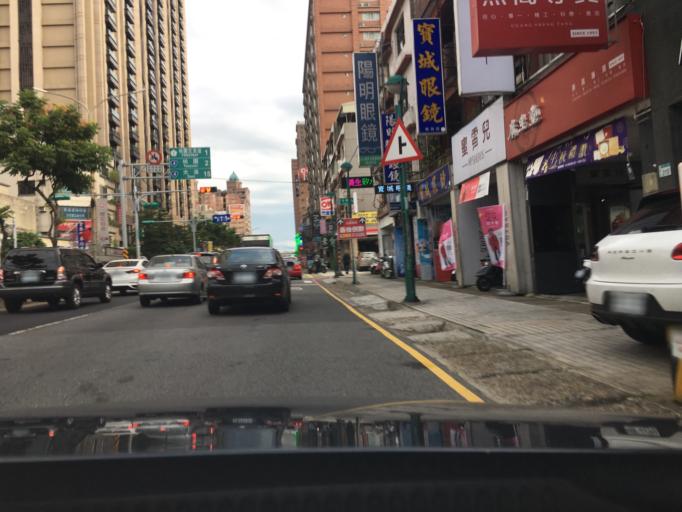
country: TW
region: Taiwan
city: Taoyuan City
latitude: 25.0463
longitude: 121.2926
